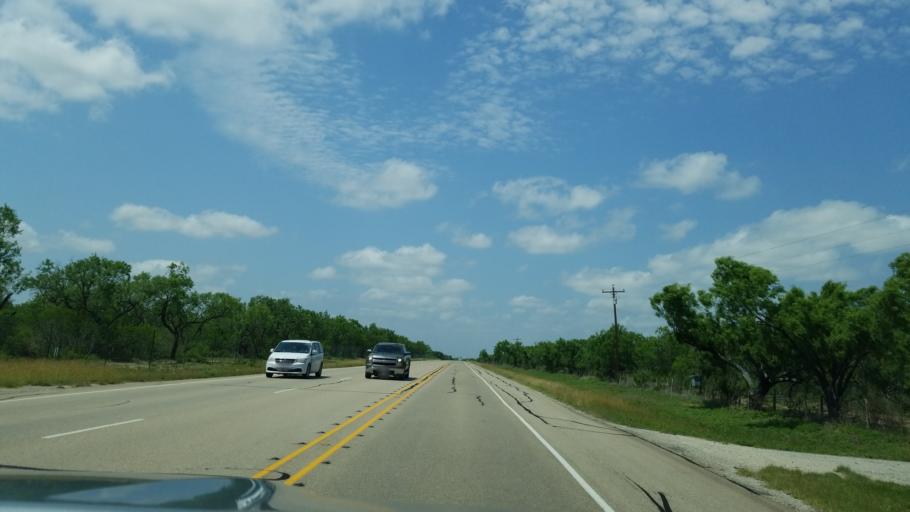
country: US
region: Texas
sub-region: Frio County
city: Pearsall
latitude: 29.0055
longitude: -99.2129
